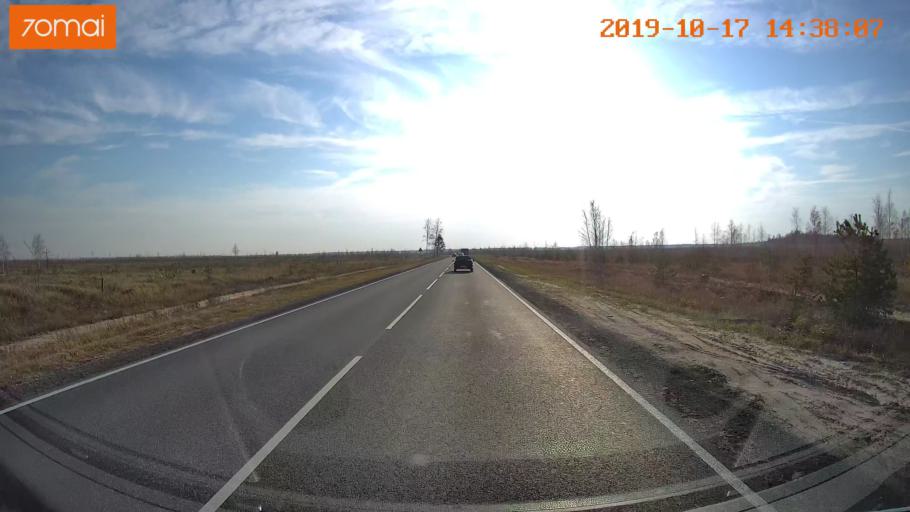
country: RU
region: Rjazan
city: Solotcha
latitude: 54.8738
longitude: 39.9872
